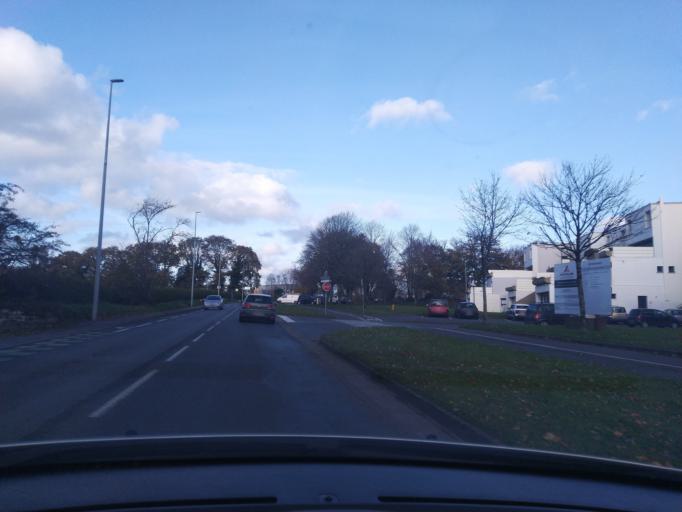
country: FR
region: Brittany
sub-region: Departement du Finistere
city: Morlaix
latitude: 48.5861
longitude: -3.8151
